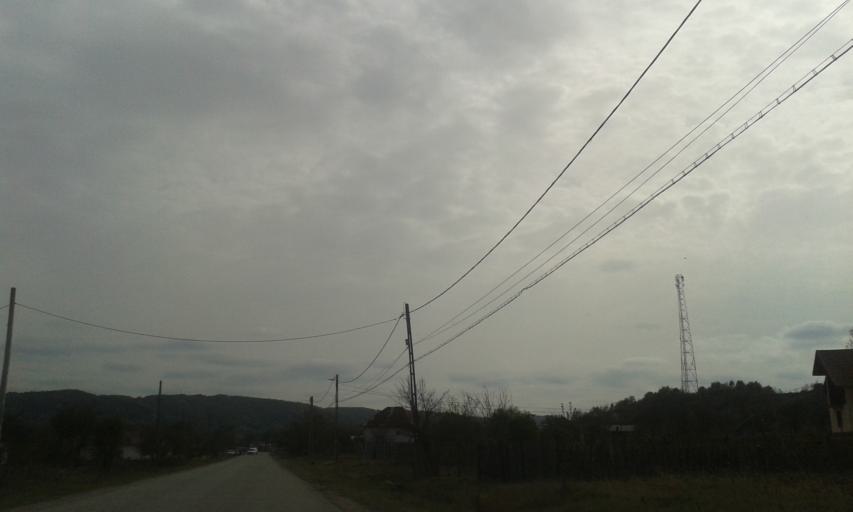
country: RO
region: Gorj
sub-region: Comuna Hurezani
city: Hurezani
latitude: 44.8200
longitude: 23.6508
